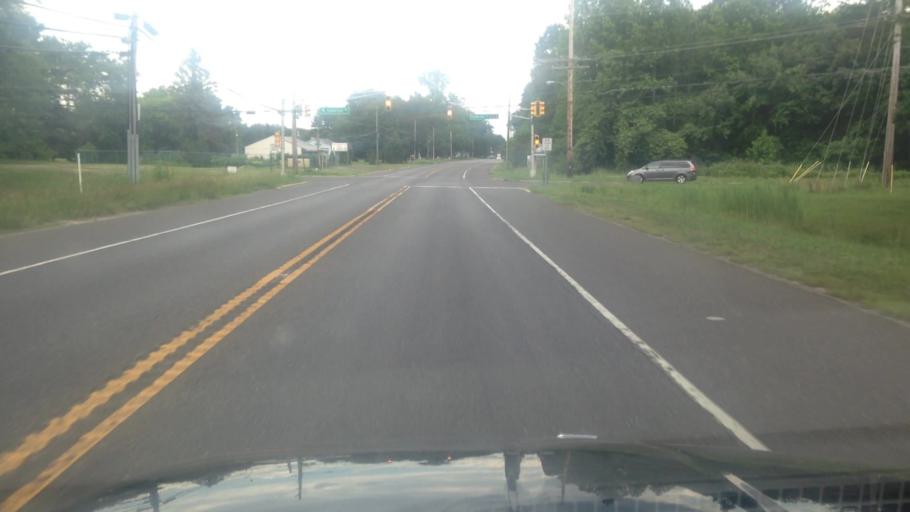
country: US
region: New Jersey
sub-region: Burlington County
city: Medford Lakes
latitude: 39.8182
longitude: -74.7351
